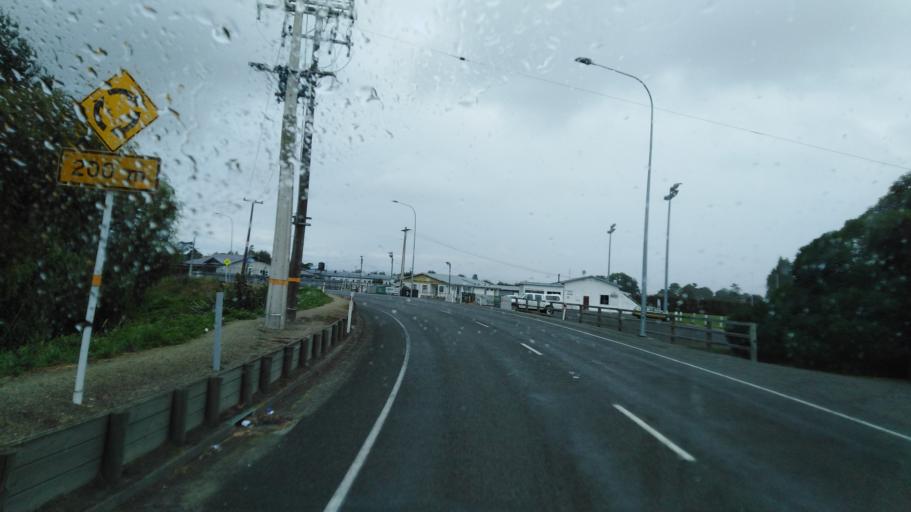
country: NZ
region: Marlborough
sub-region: Marlborough District
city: Blenheim
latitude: -41.4602
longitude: 173.9599
